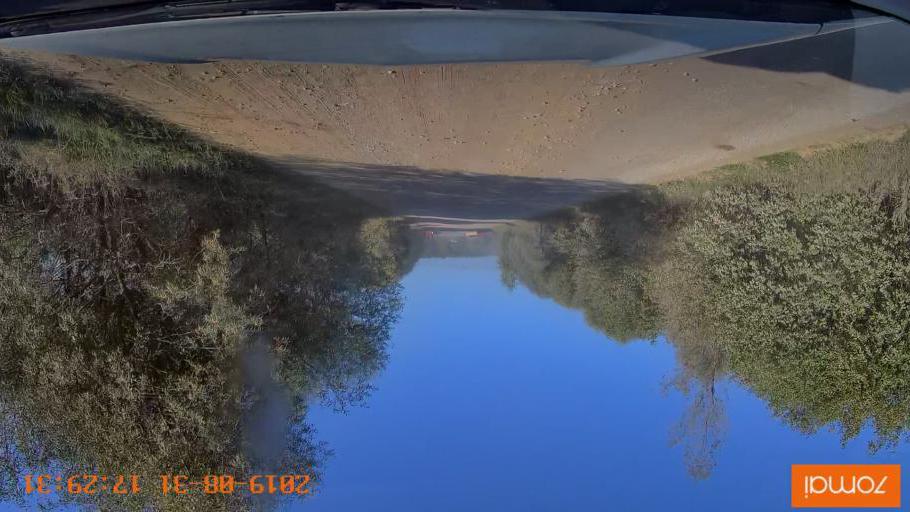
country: RU
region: Kaluga
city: Detchino
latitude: 54.8129
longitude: 36.3262
